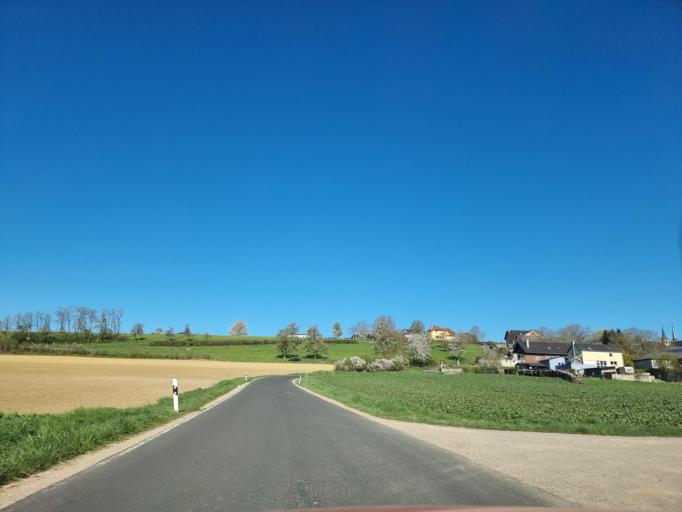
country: DE
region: Rheinland-Pfalz
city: Idenheim
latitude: 49.8953
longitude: 6.5733
